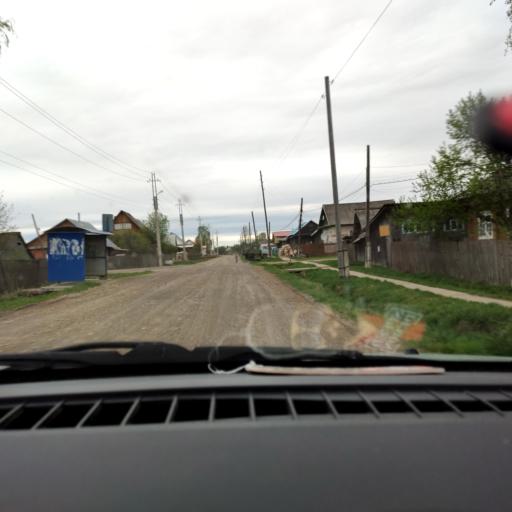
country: RU
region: Perm
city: Kudymkar
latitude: 59.0125
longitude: 54.6295
